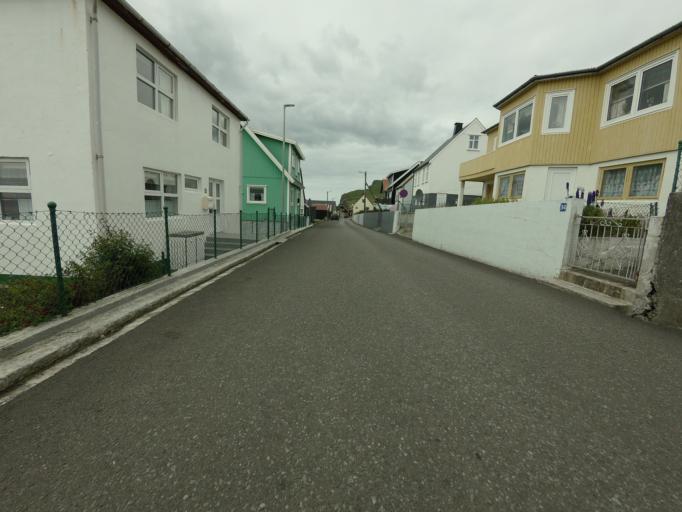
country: FO
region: Suduroy
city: Vagur
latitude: 61.4037
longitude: -6.7135
